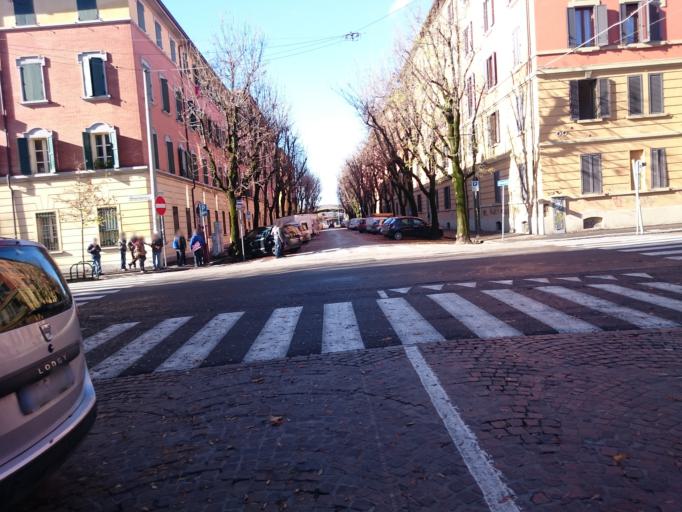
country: IT
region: Emilia-Romagna
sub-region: Provincia di Bologna
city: Bologna
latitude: 44.5105
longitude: 11.3431
